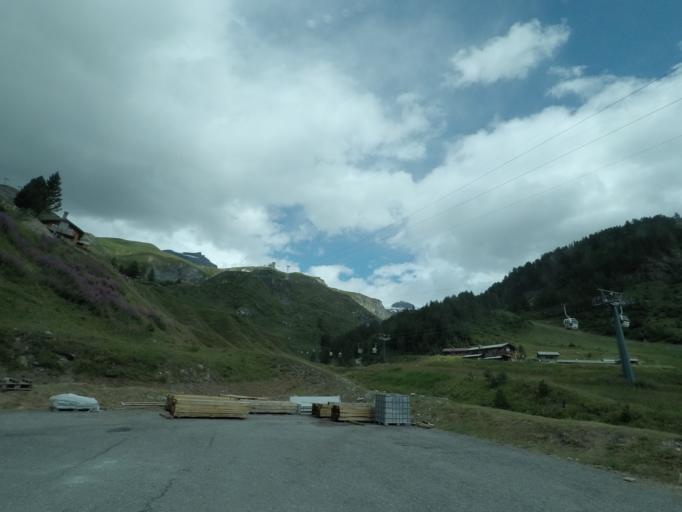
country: IT
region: Aosta Valley
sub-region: Valle d'Aosta
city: Paquier
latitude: 45.9356
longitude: 7.6360
